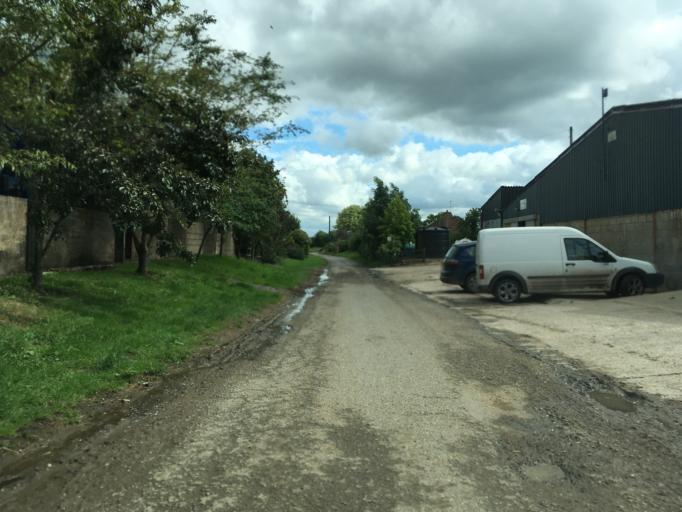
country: GB
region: England
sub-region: Gloucestershire
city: Gloucester
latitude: 51.8478
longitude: -2.3392
